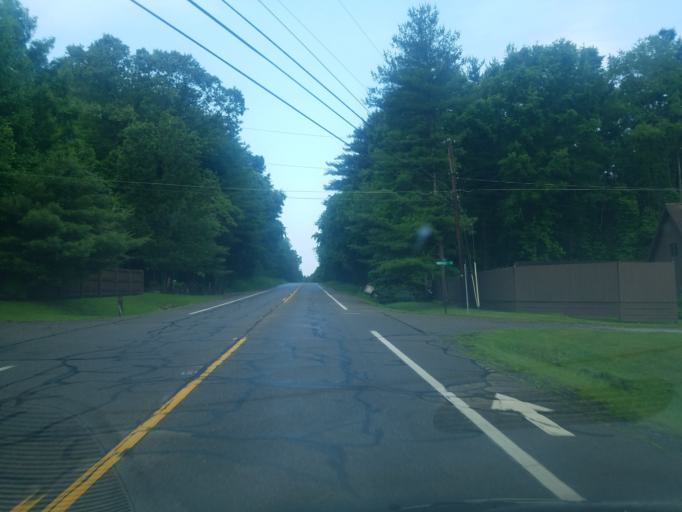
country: US
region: Ohio
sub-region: Carroll County
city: Lake Mohawk
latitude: 40.5529
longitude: -81.2207
